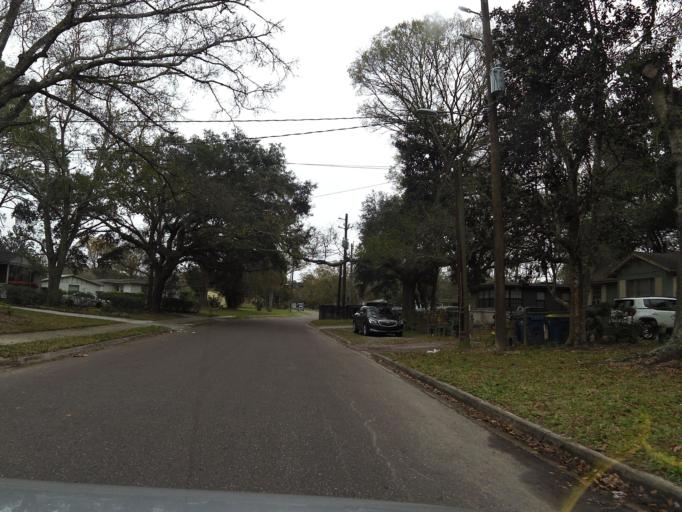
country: US
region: Florida
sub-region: Duval County
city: Jacksonville
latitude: 30.3682
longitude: -81.7022
